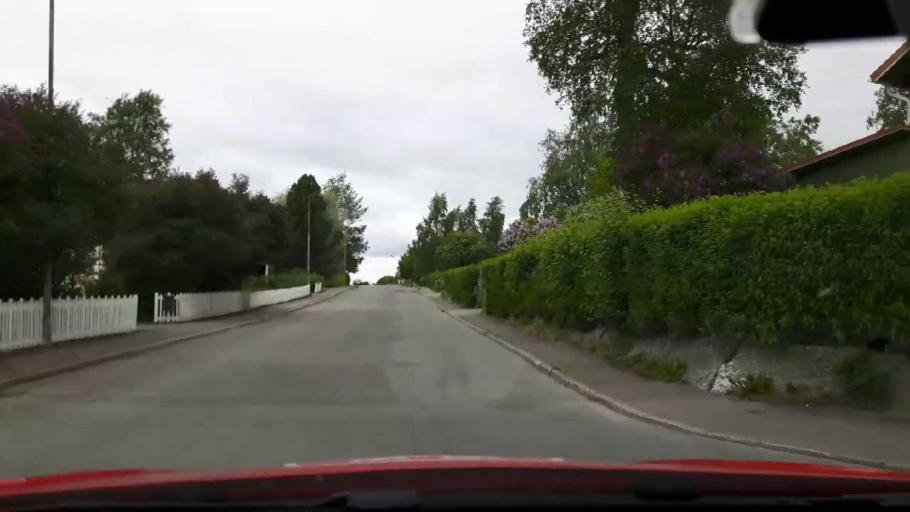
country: SE
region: Jaemtland
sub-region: OEstersunds Kommun
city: Ostersund
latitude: 63.2024
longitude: 14.6345
